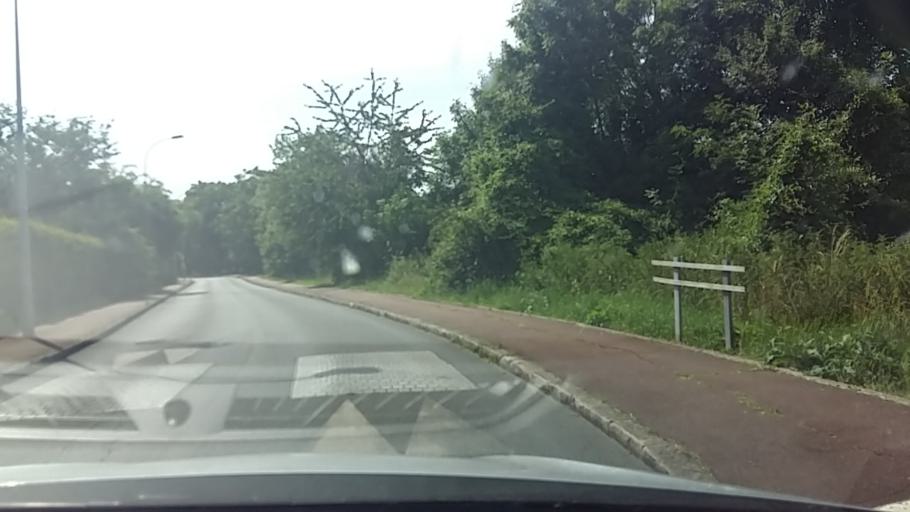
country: FR
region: Ile-de-France
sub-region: Departement du Val-de-Marne
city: Noiseau
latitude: 48.7775
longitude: 2.5393
